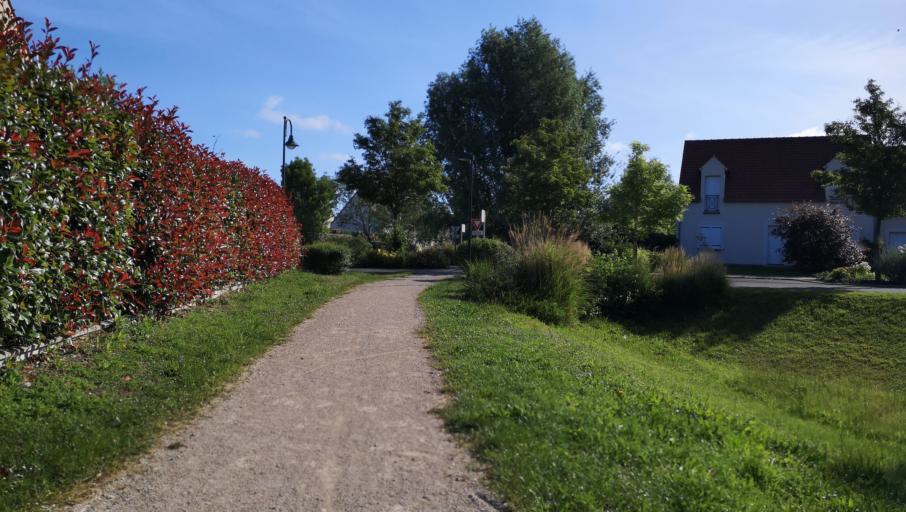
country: FR
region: Centre
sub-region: Departement du Loiret
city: Saint-Jean-de-Braye
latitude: 47.9185
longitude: 1.9736
